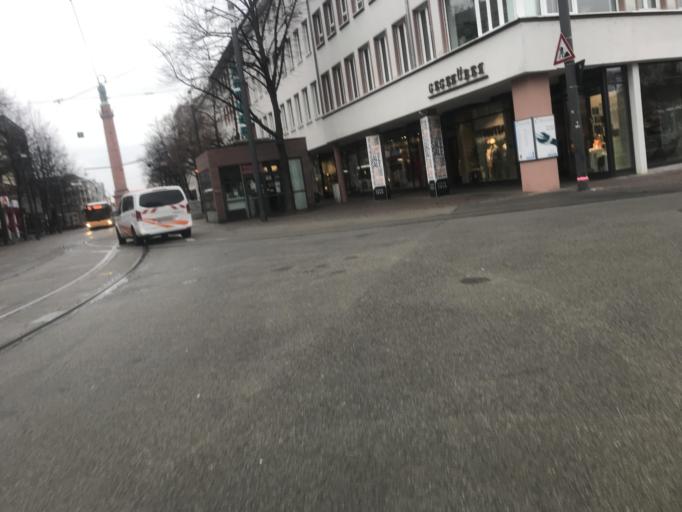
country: DE
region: Hesse
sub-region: Regierungsbezirk Darmstadt
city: Darmstadt
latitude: 49.8732
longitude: 8.6536
